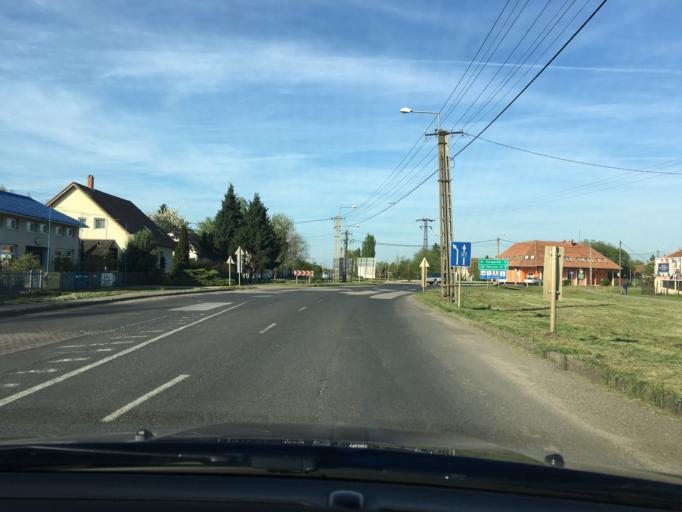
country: HU
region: Bekes
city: Szeghalom
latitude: 47.0168
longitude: 21.1538
